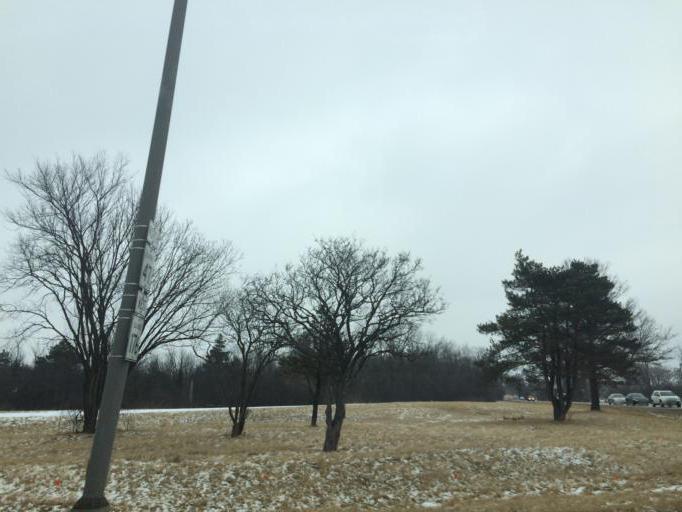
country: US
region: Illinois
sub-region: McHenry County
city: Lakewood
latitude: 42.2455
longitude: -88.4230
